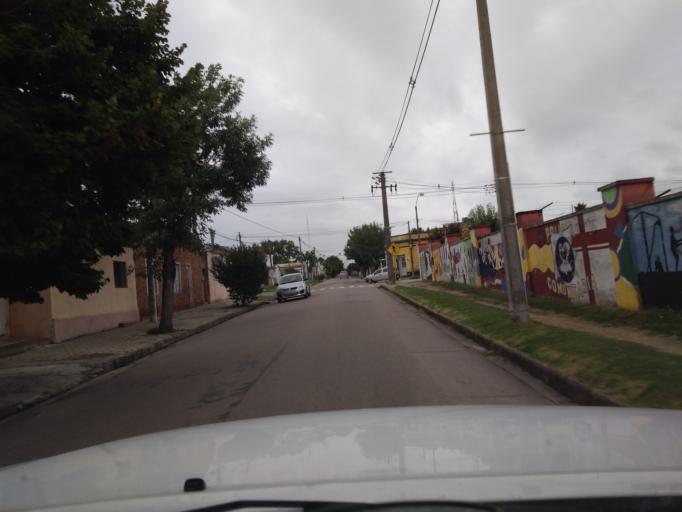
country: UY
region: Florida
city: Florida
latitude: -34.1050
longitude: -56.2089
